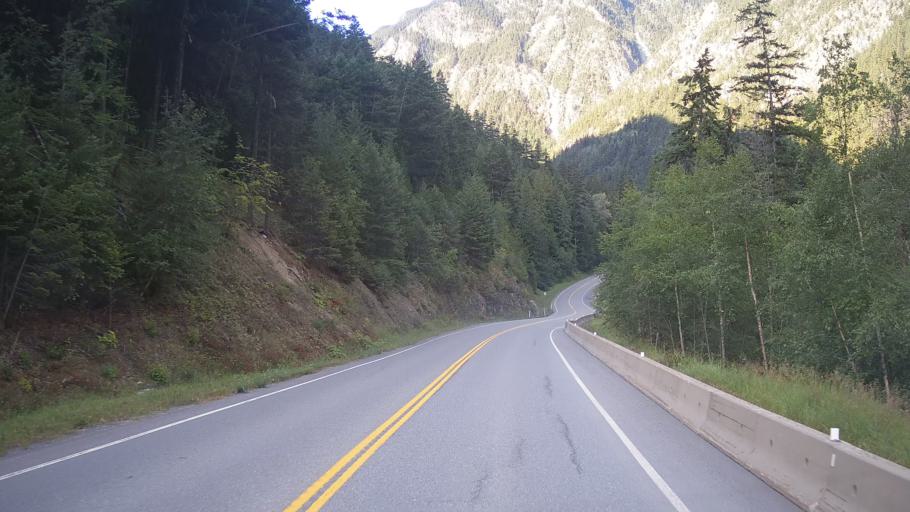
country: CA
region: British Columbia
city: Lillooet
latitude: 50.6276
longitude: -122.0957
